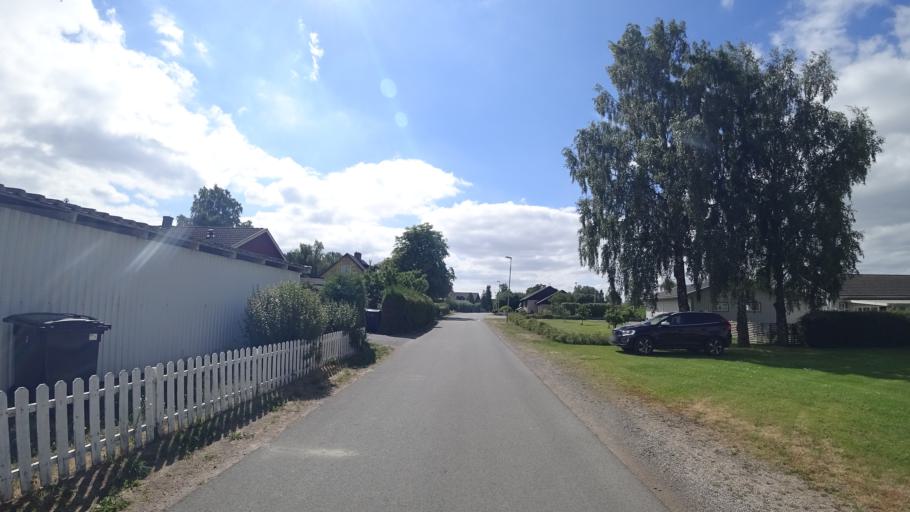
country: SE
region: Skane
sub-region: Kristianstads Kommun
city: Ahus
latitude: 55.9793
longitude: 14.2751
